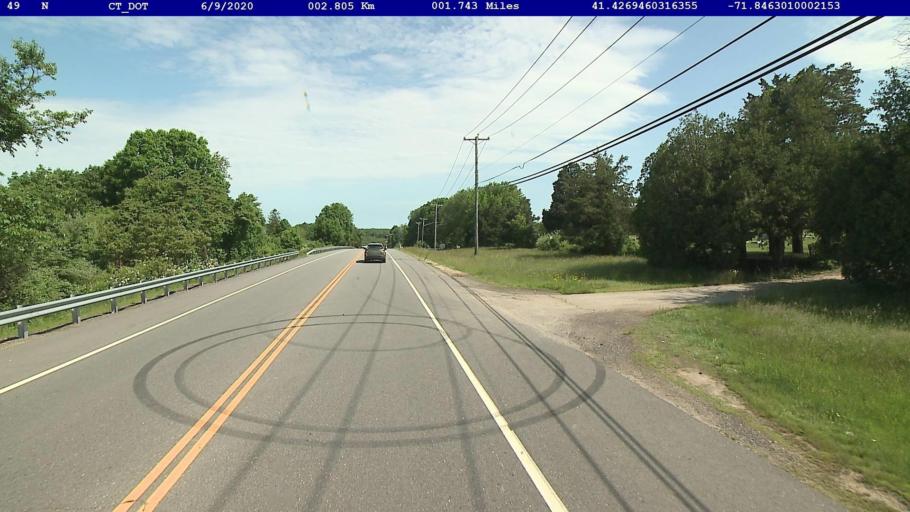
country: US
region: Connecticut
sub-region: New London County
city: Pawcatuck
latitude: 41.4270
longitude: -71.8463
